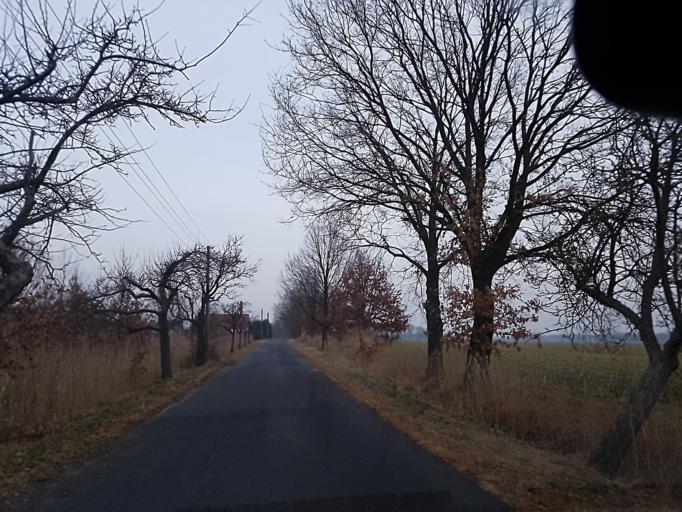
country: DE
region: Brandenburg
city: Ruckersdorf
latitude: 51.5719
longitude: 13.5434
